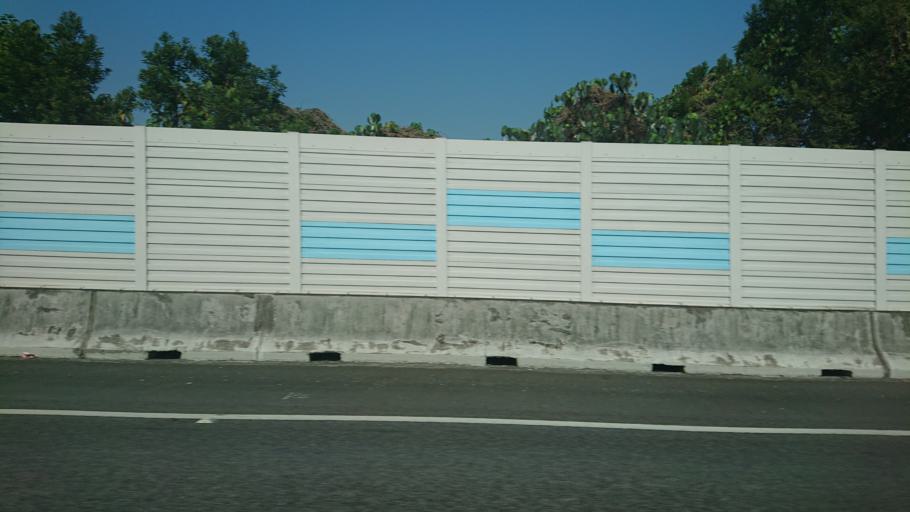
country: TW
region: Taiwan
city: Lugu
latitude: 23.7790
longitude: 120.6995
